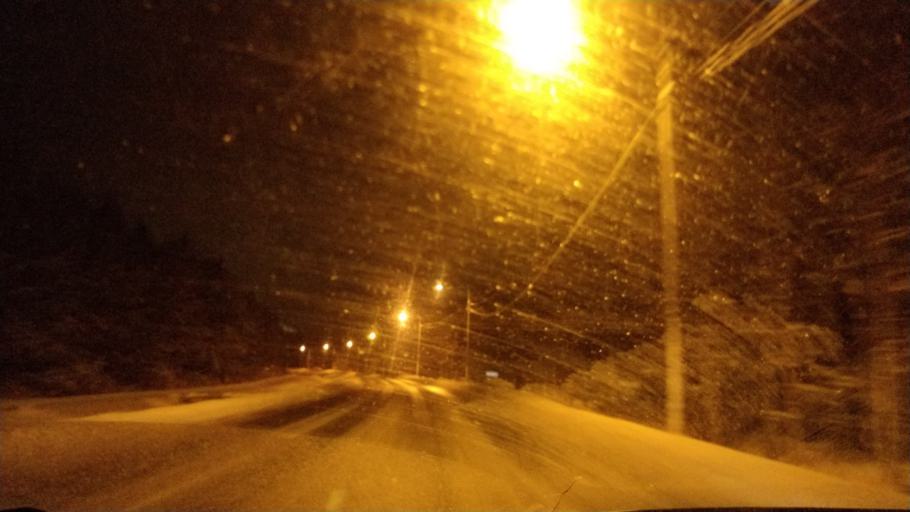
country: FI
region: Lapland
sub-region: Rovaniemi
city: Rovaniemi
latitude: 66.3875
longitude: 25.3772
